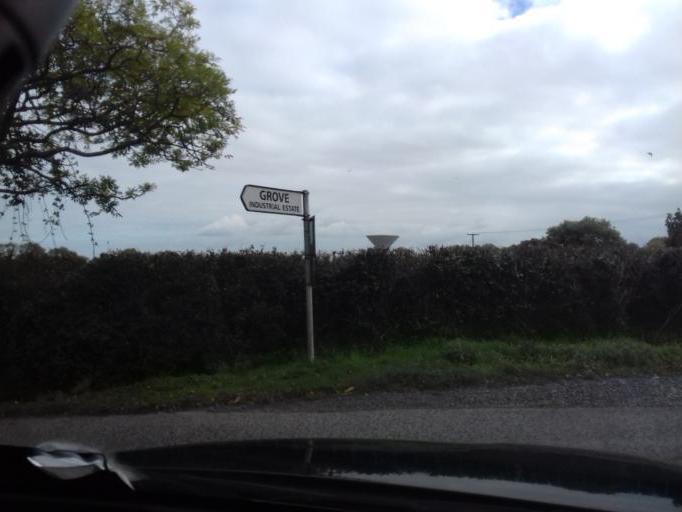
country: IE
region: Leinster
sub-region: Dublin City
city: Finglas
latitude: 53.4110
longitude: -6.2986
